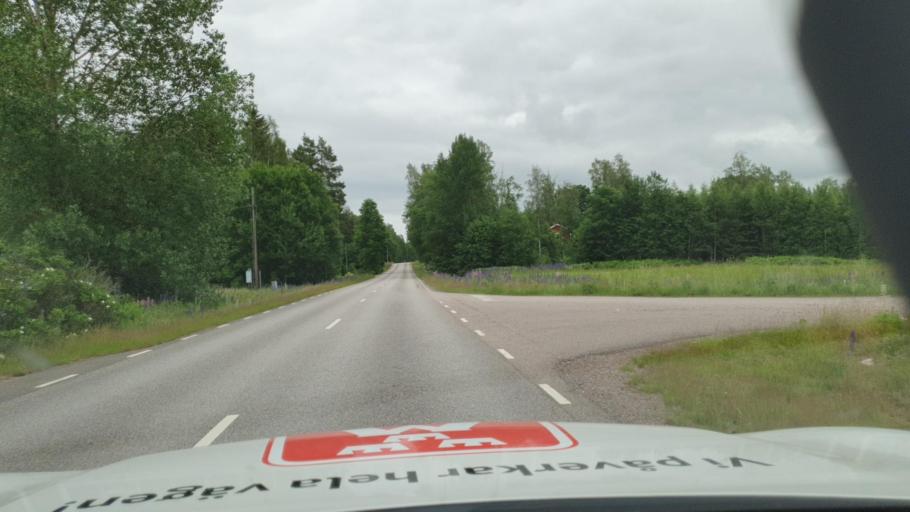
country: SE
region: Vaermland
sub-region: Sunne Kommun
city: Sunne
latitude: 59.8051
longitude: 13.0405
